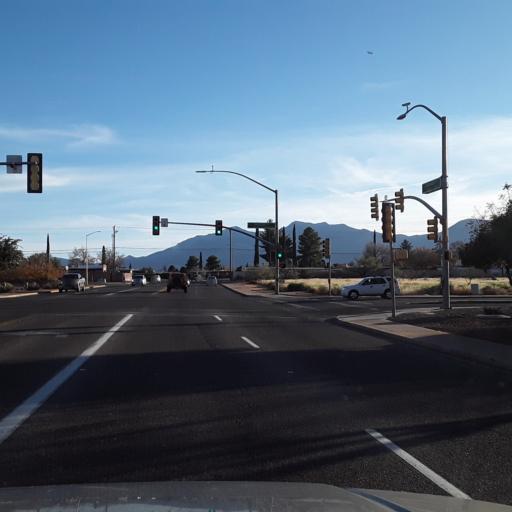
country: US
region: Arizona
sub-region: Cochise County
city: Sierra Vista
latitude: 31.5526
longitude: -110.2776
